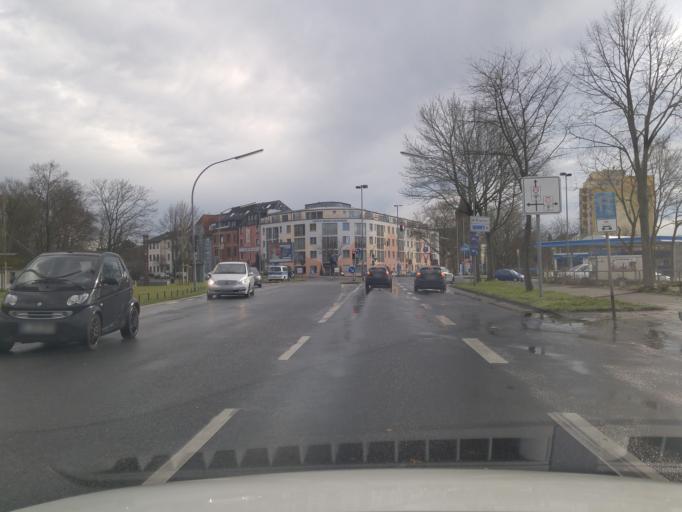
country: DE
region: North Rhine-Westphalia
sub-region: Regierungsbezirk Koln
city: Buchheim
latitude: 50.9437
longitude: 7.0280
